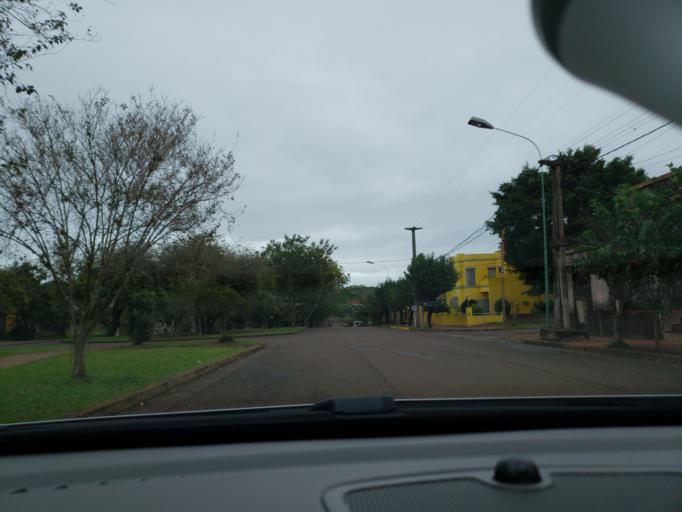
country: AR
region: Misiones
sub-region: Departamento de Apostoles
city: Apostoles
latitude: -27.9113
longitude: -55.7520
